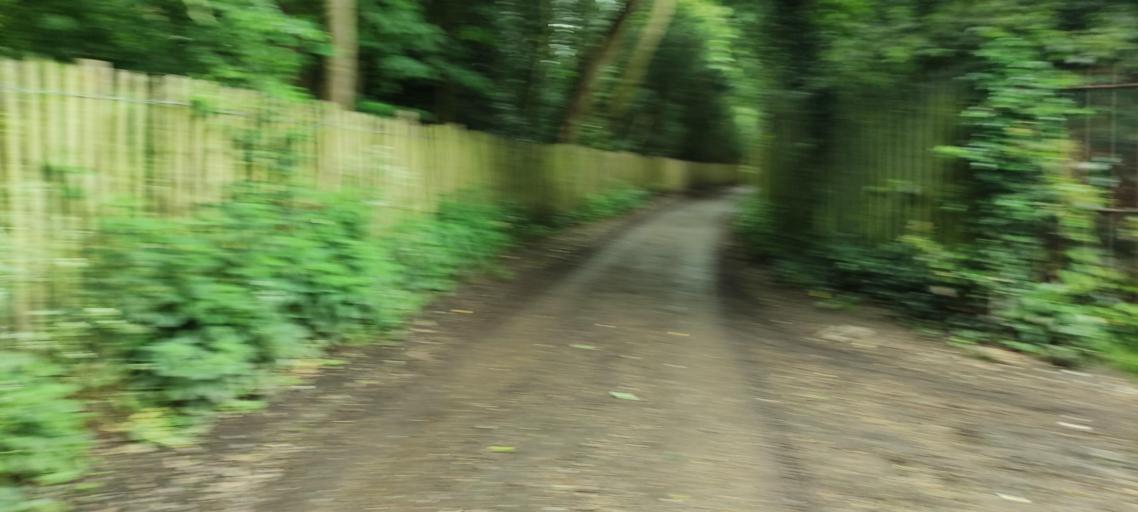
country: GB
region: England
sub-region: Greater London
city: Chislehurst
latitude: 51.4048
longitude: 0.0711
